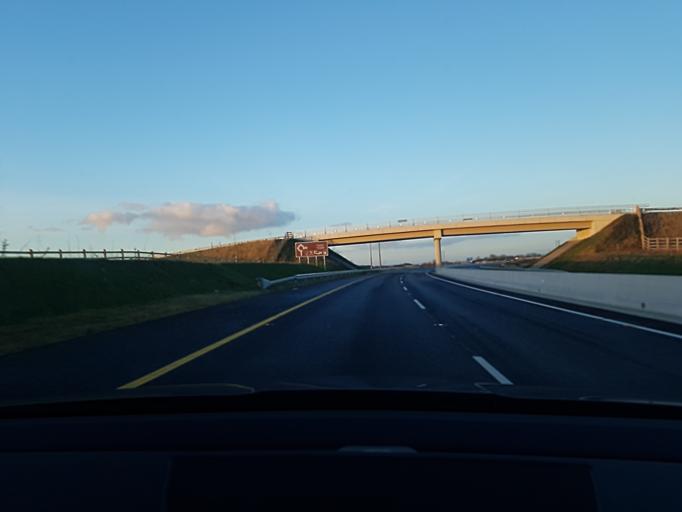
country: IE
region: Connaught
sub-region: County Galway
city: Tuam
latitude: 53.4984
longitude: -8.8785
